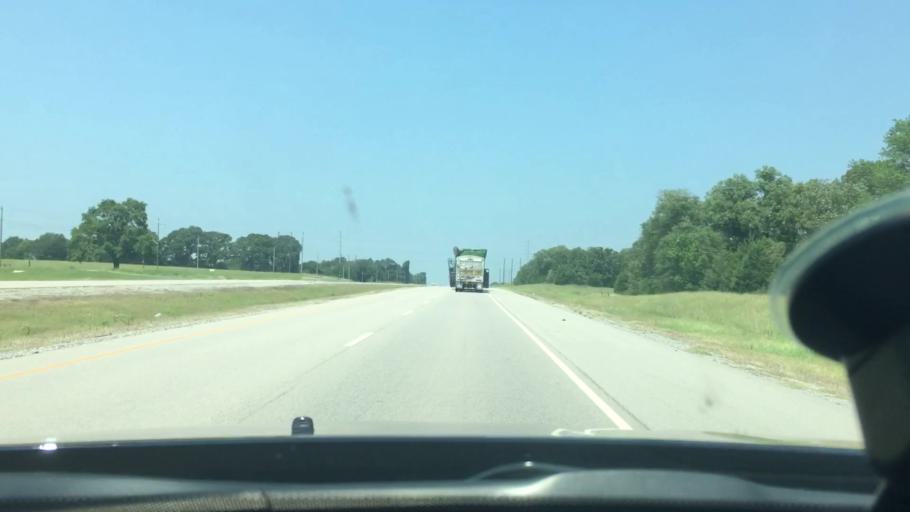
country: US
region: Oklahoma
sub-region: Atoka County
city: Atoka
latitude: 34.3270
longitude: -96.0445
